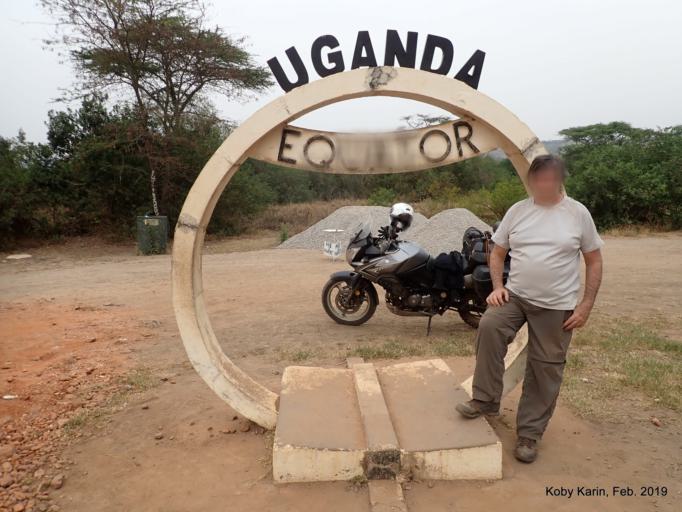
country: UG
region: Western Region
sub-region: Kasese District
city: Kilembe
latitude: -0.0027
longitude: 30.0009
